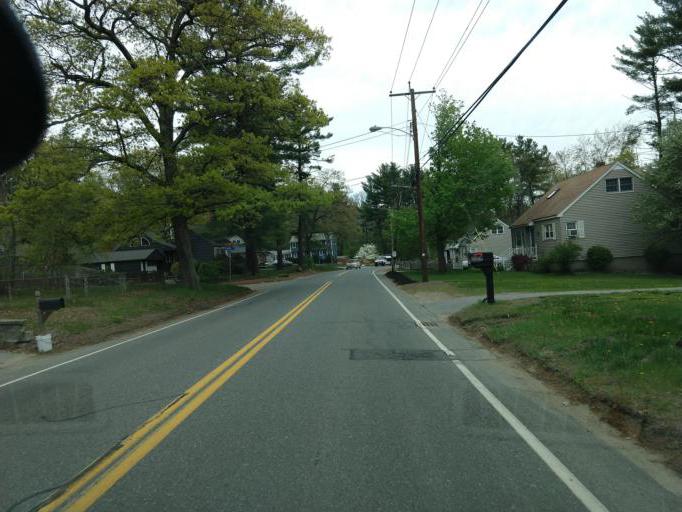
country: US
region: Massachusetts
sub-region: Middlesex County
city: Tewksbury
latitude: 42.6094
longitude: -71.1896
